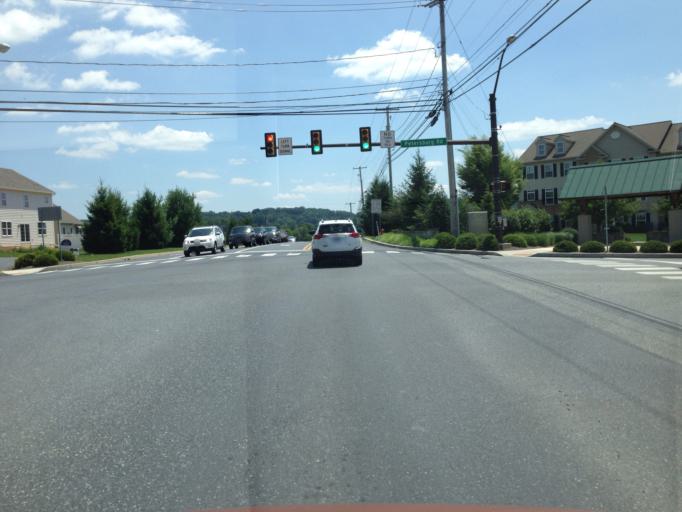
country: US
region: Pennsylvania
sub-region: Lancaster County
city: East Petersburg
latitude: 40.1054
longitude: -76.3323
